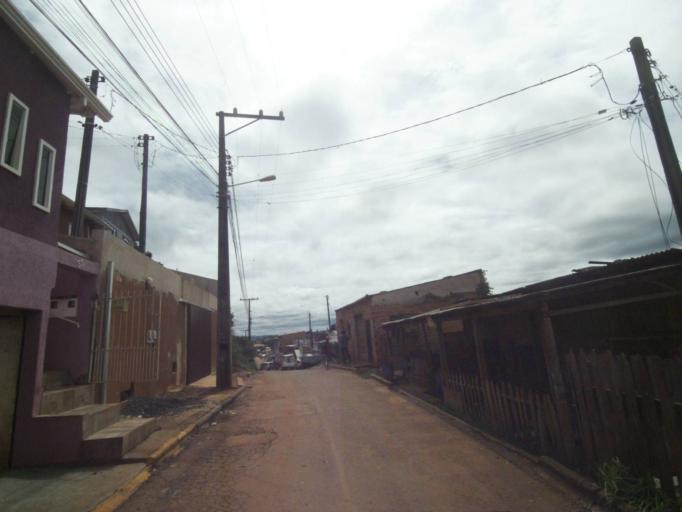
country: BR
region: Parana
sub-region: Telemaco Borba
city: Telemaco Borba
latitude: -24.3310
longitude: -50.6379
